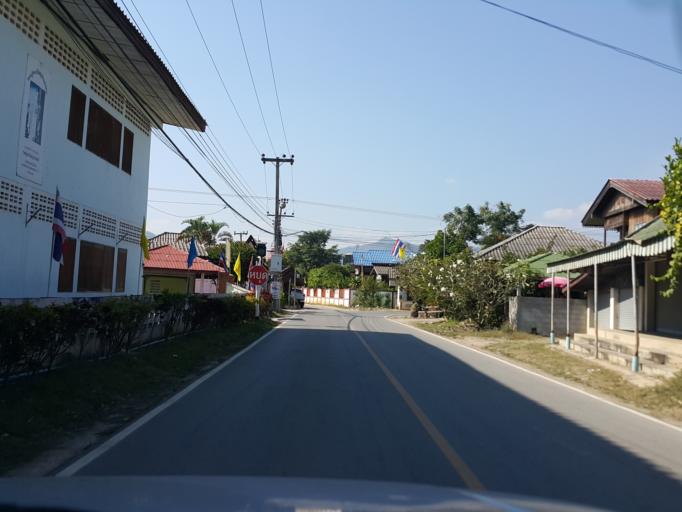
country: TH
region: Chiang Mai
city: Mae Wang
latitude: 18.5898
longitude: 98.7963
